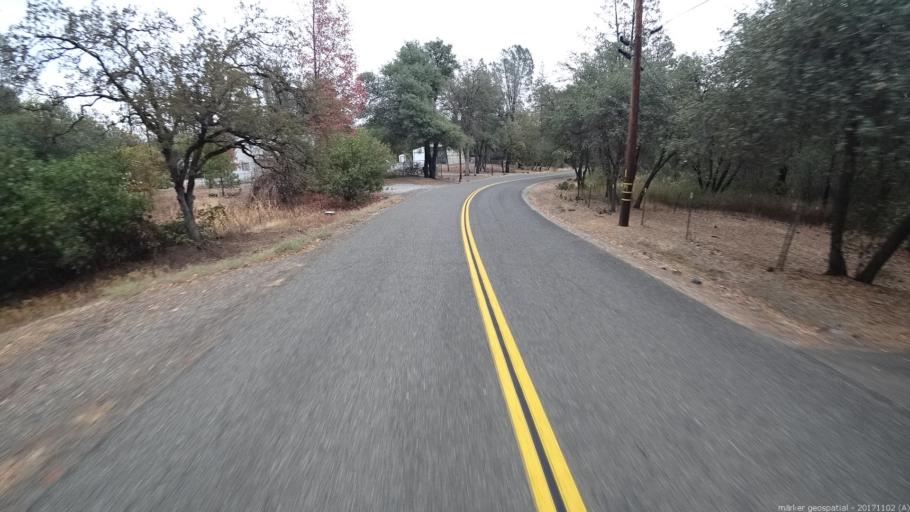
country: US
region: California
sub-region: Shasta County
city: Central Valley (historical)
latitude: 40.6648
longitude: -122.4053
